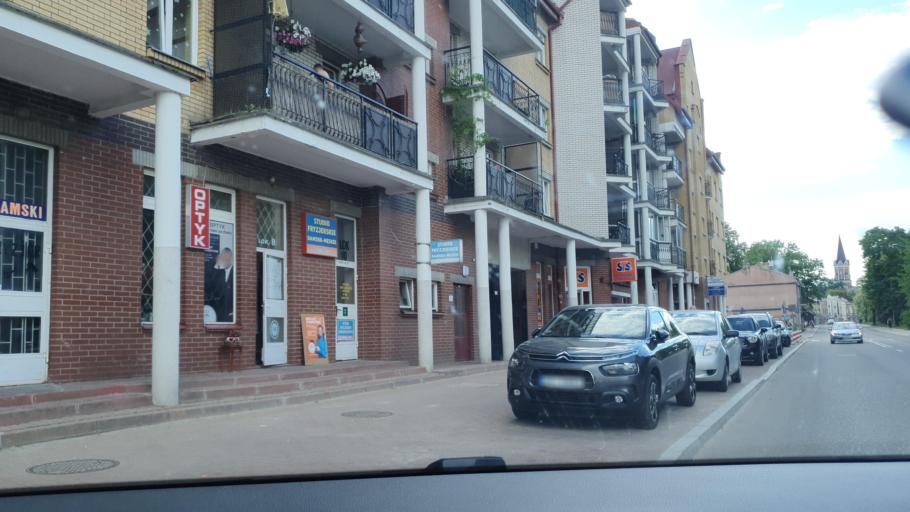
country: PL
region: Podlasie
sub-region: Bialystok
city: Bialystok
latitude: 53.1280
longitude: 23.1800
